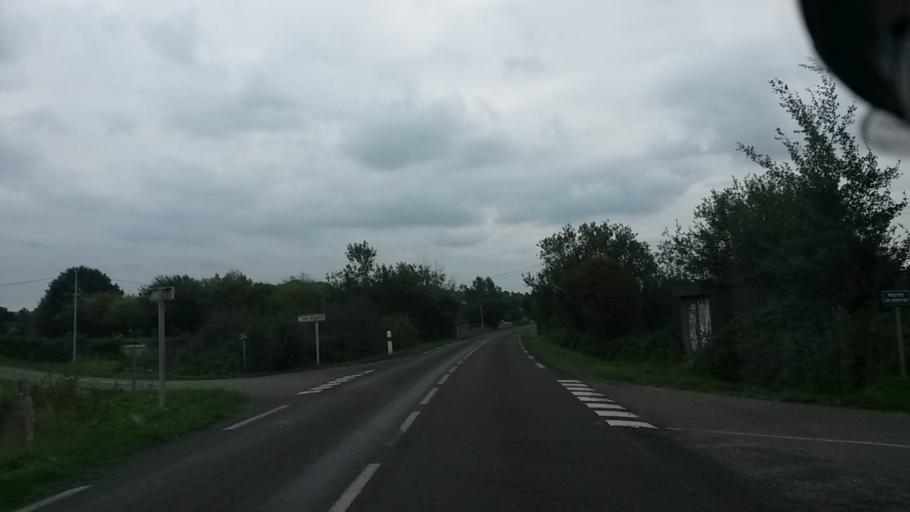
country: FR
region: Haute-Normandie
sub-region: Departement de la Seine-Maritime
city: Forges-les-Eaux
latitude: 49.5788
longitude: 1.5436
